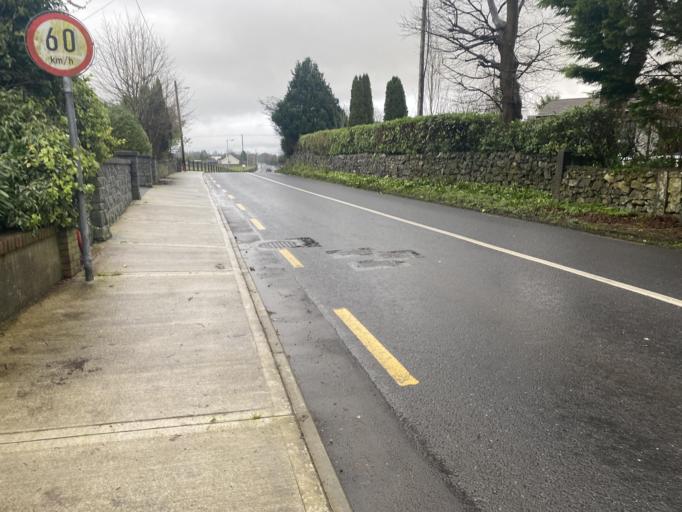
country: IE
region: Connaught
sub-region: County Galway
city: Tuam
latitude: 53.5195
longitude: -8.8363
